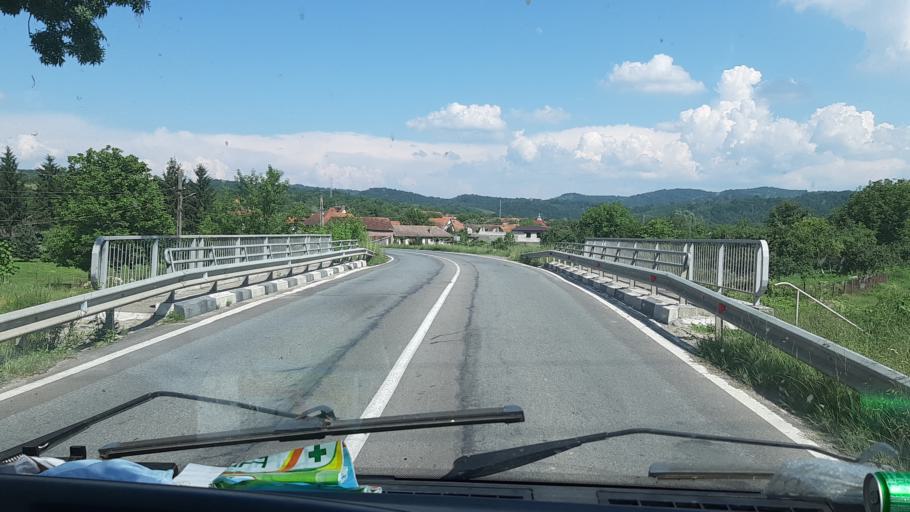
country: RO
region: Caras-Severin
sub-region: Comuna Ezeris
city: Ezeris
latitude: 45.3769
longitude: 21.9361
